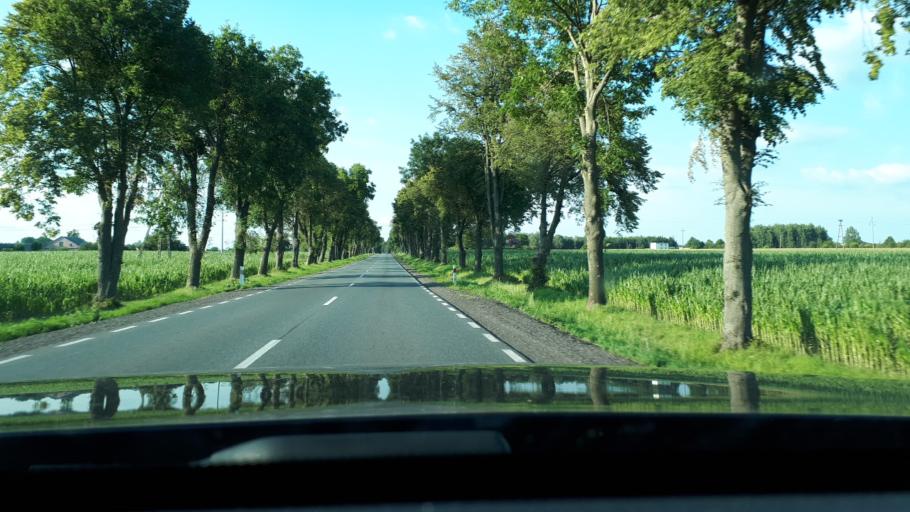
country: PL
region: Masovian Voivodeship
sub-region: Powiat ciechanowski
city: Ciechanow
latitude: 52.8227
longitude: 20.6150
